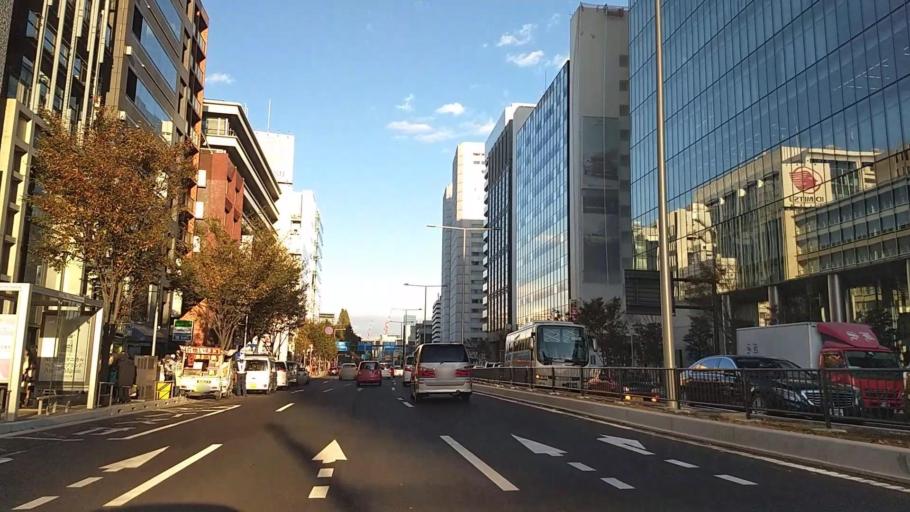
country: JP
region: Tokyo
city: Tokyo
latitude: 35.6719
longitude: 139.7216
